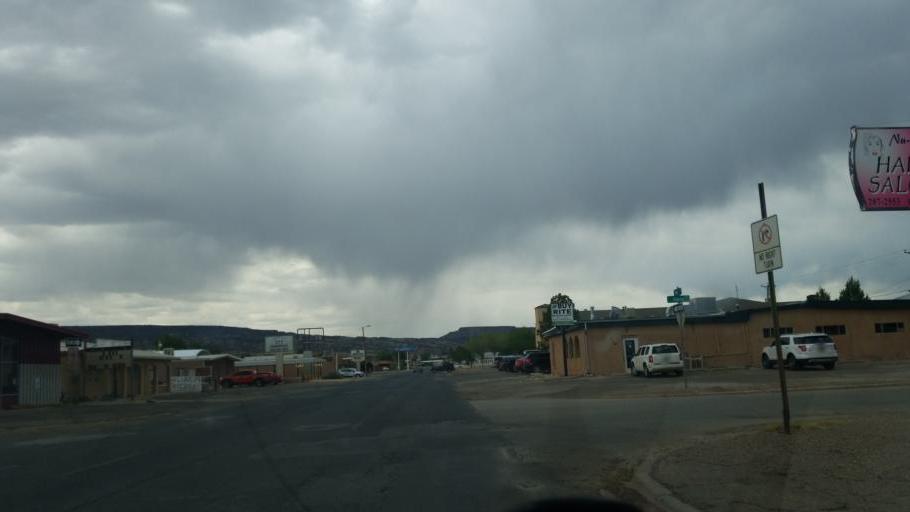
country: US
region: New Mexico
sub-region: Cibola County
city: Grants
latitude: 35.1576
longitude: -107.8438
